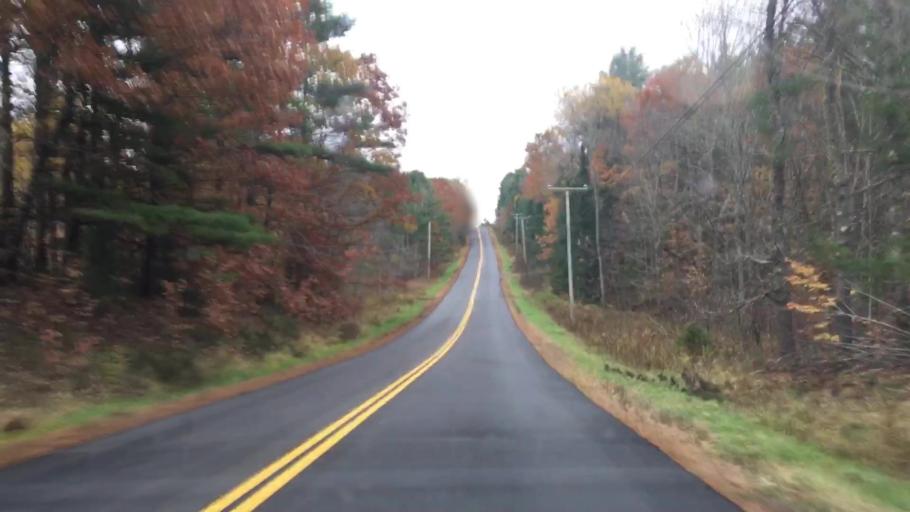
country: US
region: Maine
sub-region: Kennebec County
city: Pittston
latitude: 44.1675
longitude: -69.7032
